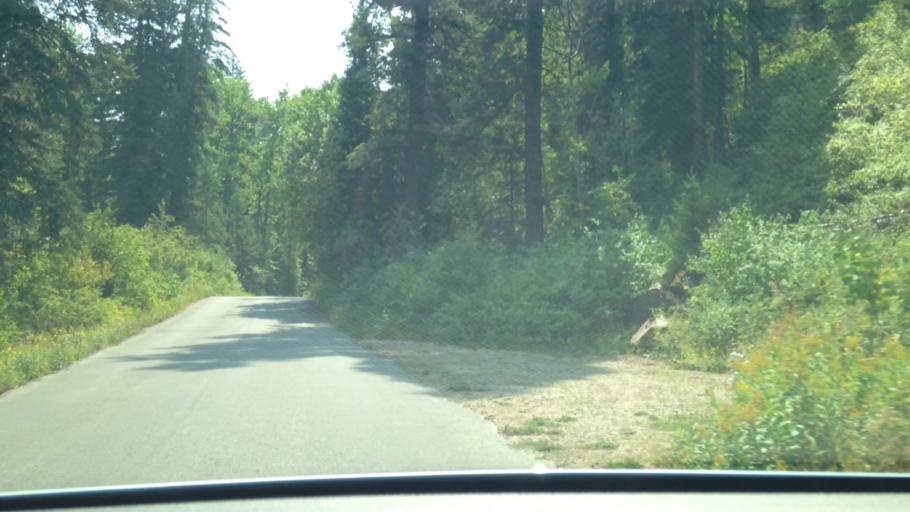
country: US
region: Utah
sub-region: Summit County
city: Summit Park
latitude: 40.6986
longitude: -111.6836
